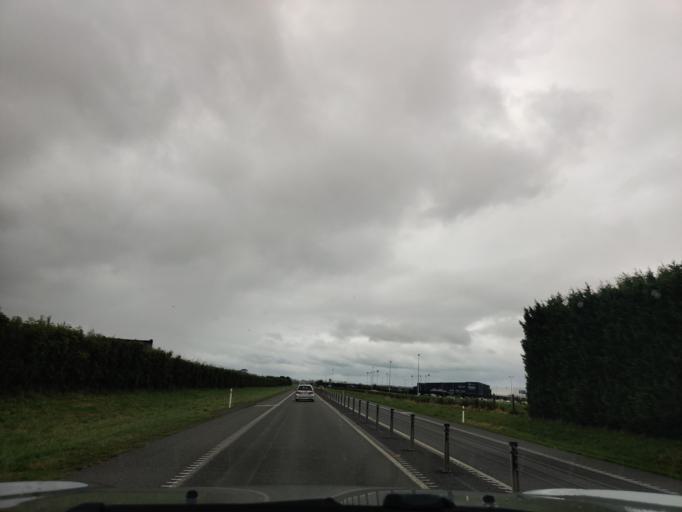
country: NZ
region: Hawke's Bay
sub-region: Hastings District
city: Hastings
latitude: -39.6129
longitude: 176.8279
